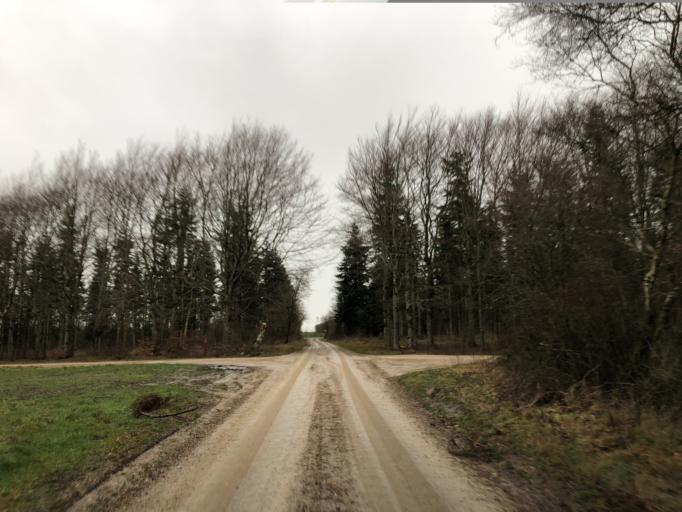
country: DK
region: Central Jutland
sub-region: Holstebro Kommune
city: Vinderup
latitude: 56.3941
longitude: 8.8700
